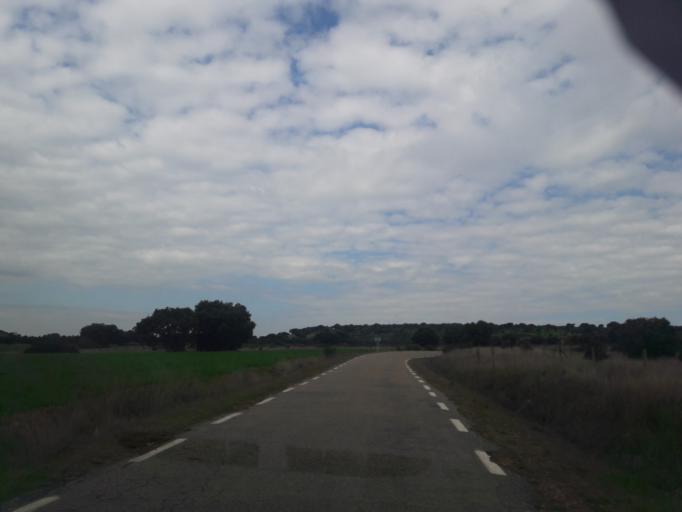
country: ES
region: Castille and Leon
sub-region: Provincia de Salamanca
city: Serradilla del Arroyo
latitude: 40.5224
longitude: -6.3779
